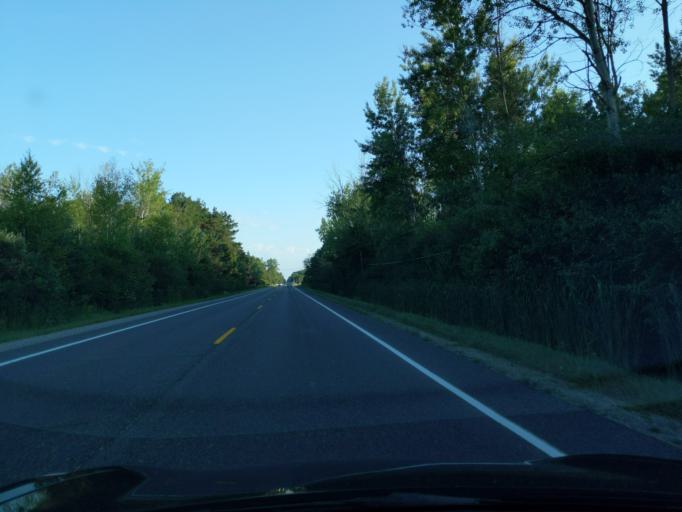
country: US
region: Michigan
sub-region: Midland County
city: Midland
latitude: 43.5741
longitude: -84.3695
